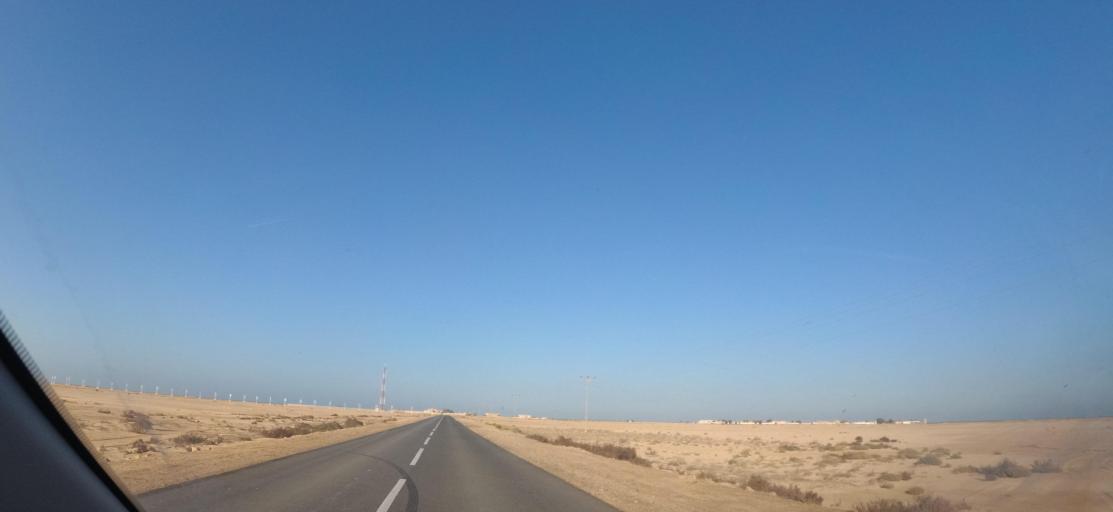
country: QA
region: Madinat ash Shamal
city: Ar Ru'ays
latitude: 26.1494
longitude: 51.2487
